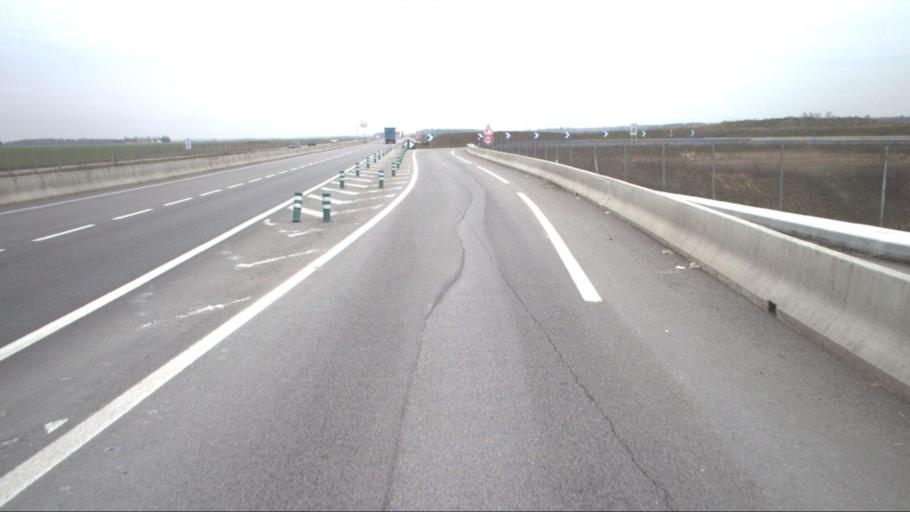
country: FR
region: Ile-de-France
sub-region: Departement des Yvelines
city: Sonchamp
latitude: 48.5795
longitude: 1.8324
